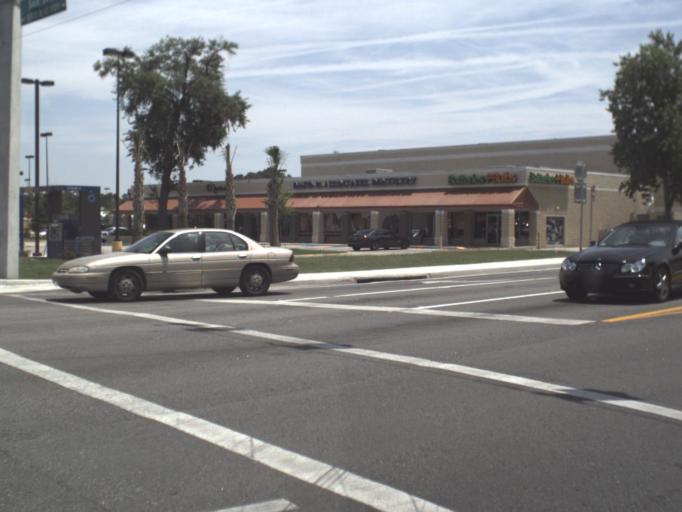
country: US
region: Florida
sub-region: Saint Johns County
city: Fruit Cove
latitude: 30.1752
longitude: -81.6278
